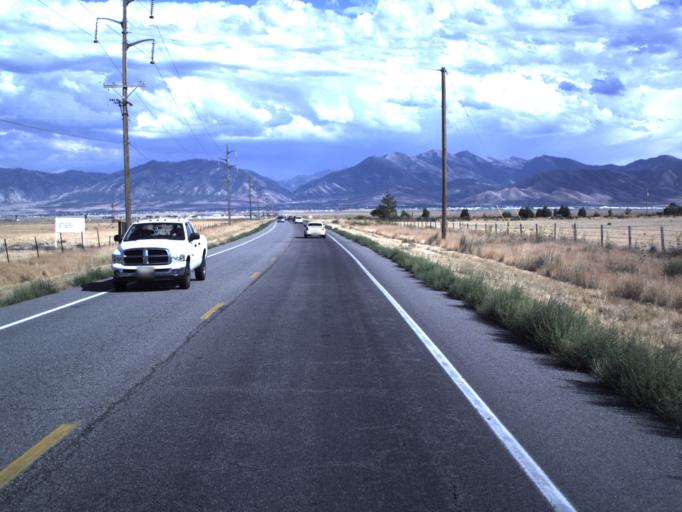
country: US
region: Utah
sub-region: Tooele County
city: Grantsville
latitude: 40.5876
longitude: -112.4141
